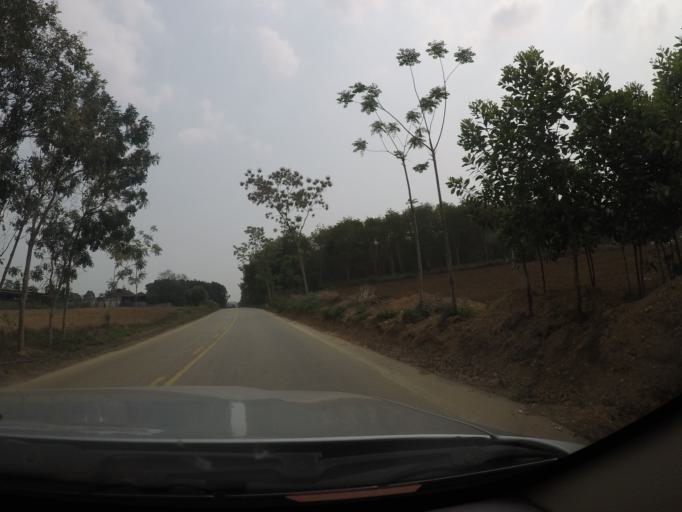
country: VN
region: Thanh Hoa
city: Thi Tran Yen Cat
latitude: 19.4928
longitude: 105.3924
